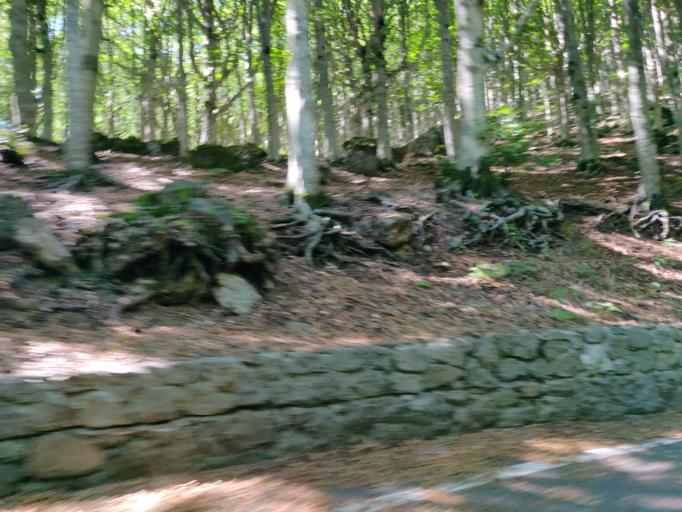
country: IT
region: Tuscany
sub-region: Provincia di Siena
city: Abbadia San Salvatore
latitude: 42.8863
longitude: 11.6254
